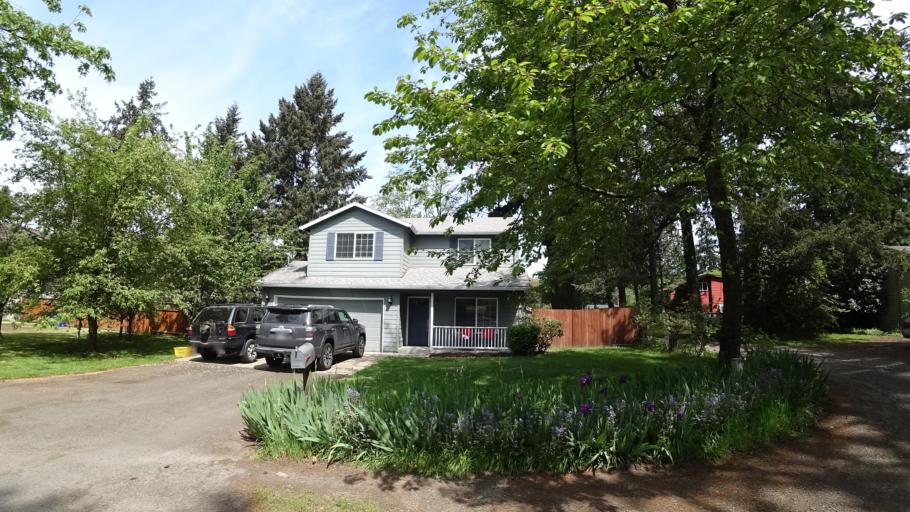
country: US
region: Oregon
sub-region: Clackamas County
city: Milwaukie
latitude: 45.4539
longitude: -122.6028
